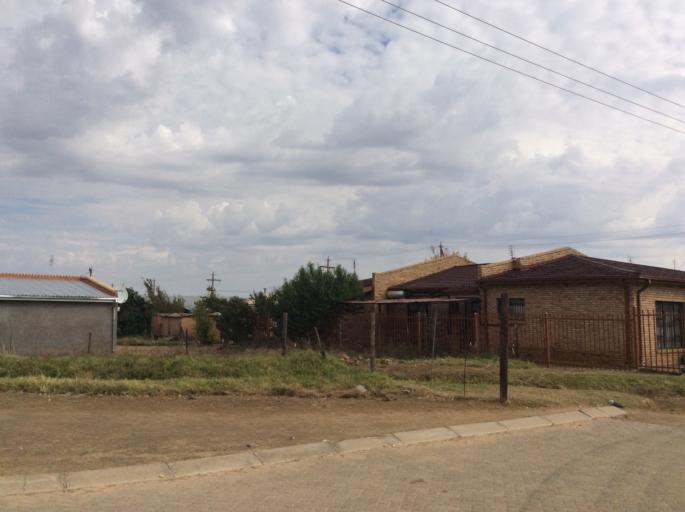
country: LS
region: Mafeteng
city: Mafeteng
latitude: -29.7187
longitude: 27.0288
